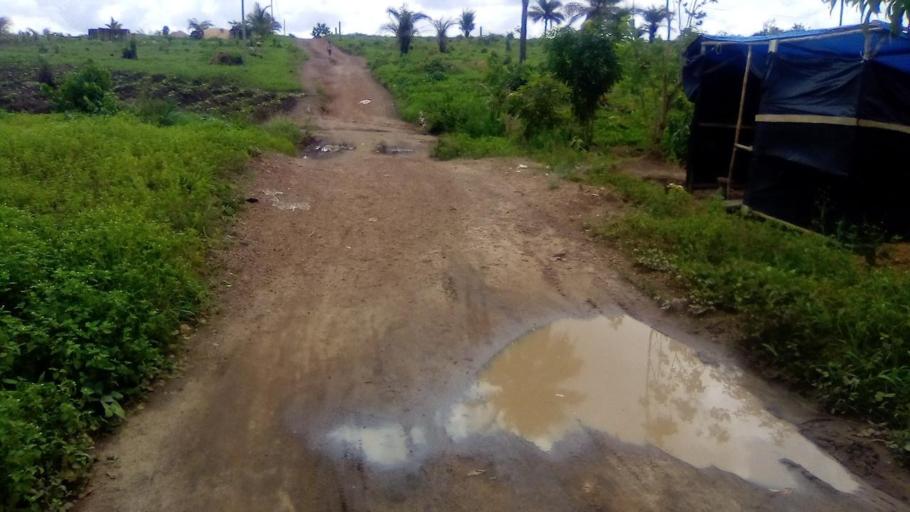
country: SL
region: Southern Province
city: Bo
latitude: 7.9331
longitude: -11.7461
